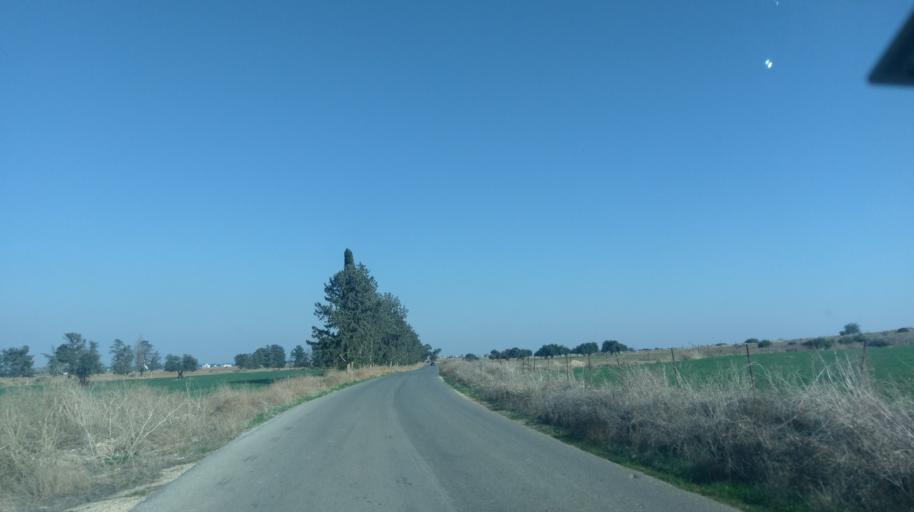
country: CY
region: Larnaka
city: Troulloi
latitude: 35.1006
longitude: 33.6490
